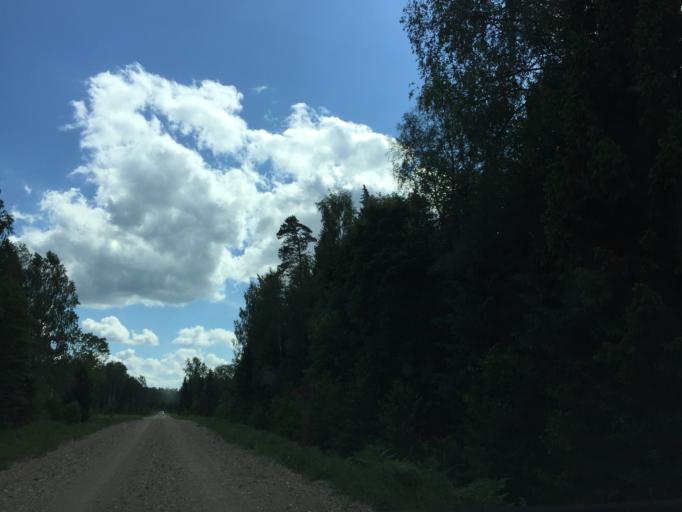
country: LV
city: Tireli
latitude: 56.8457
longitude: 23.6967
